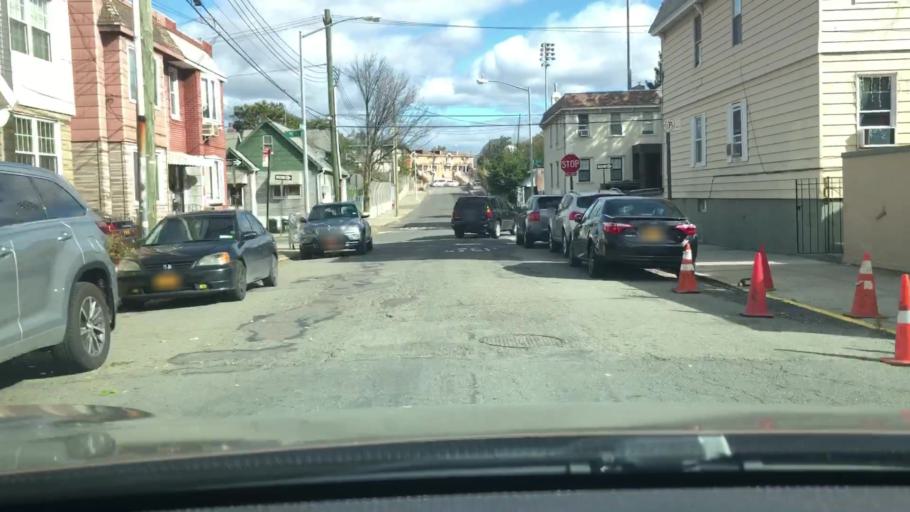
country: US
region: New York
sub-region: Queens County
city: Long Island City
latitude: 40.7142
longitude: -73.9086
